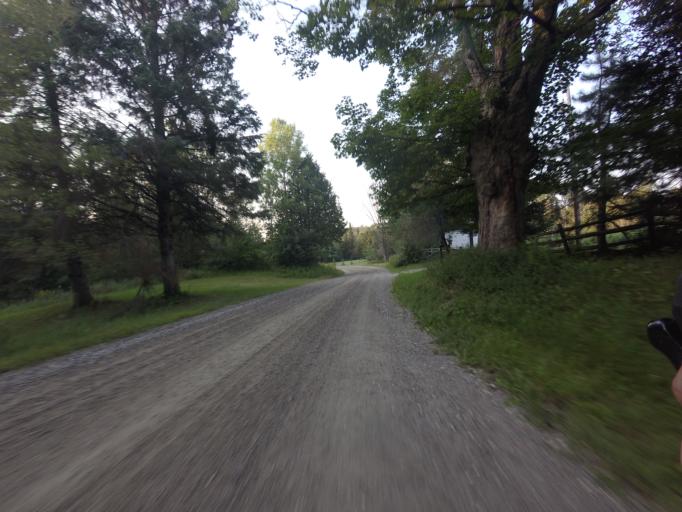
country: CA
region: Ontario
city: Renfrew
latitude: 45.0513
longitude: -76.7486
